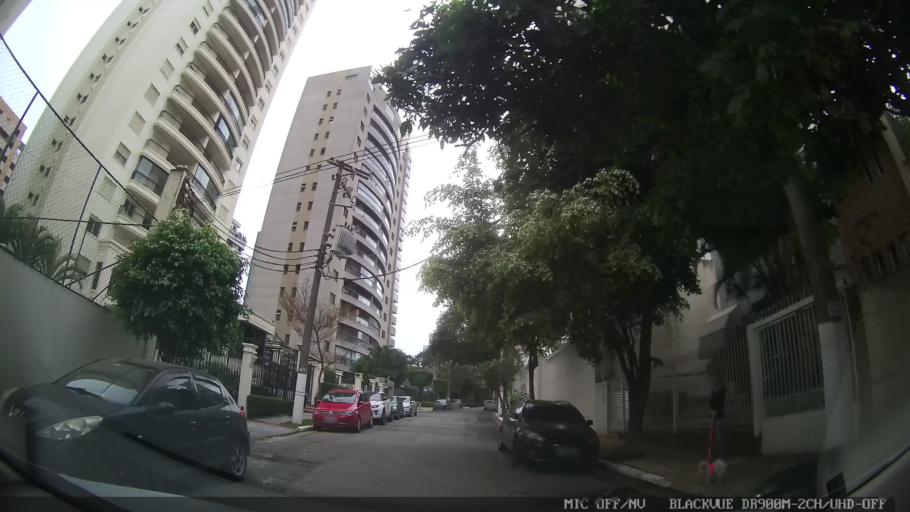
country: BR
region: Sao Paulo
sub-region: Sao Paulo
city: Sao Paulo
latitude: -23.5920
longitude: -46.6253
